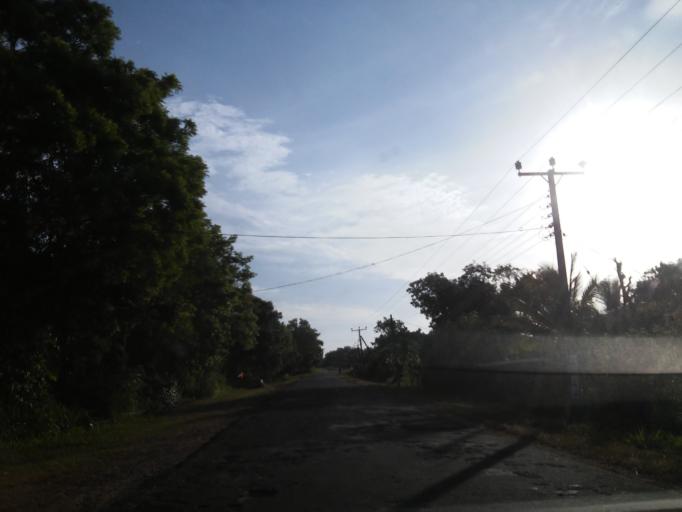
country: LK
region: Central
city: Sigiriya
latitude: 8.1707
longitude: 80.6632
